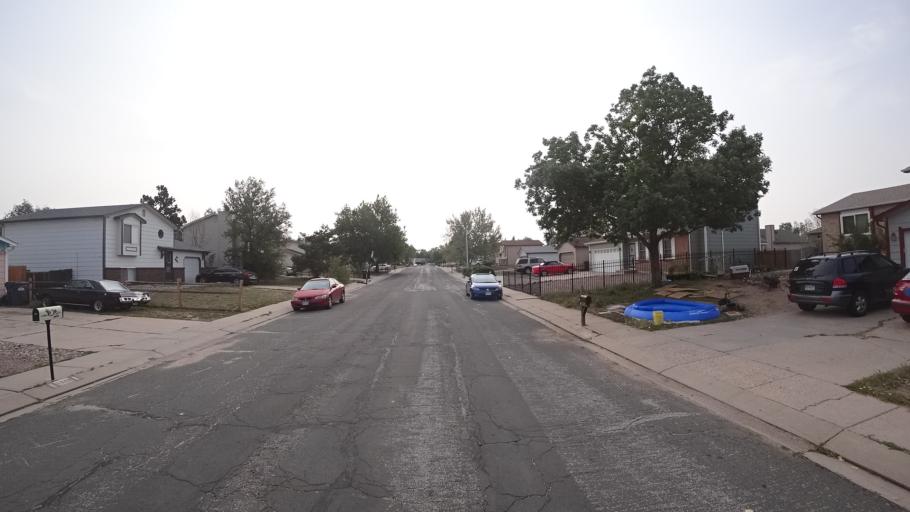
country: US
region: Colorado
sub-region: El Paso County
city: Stratmoor
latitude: 38.8131
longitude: -104.7398
